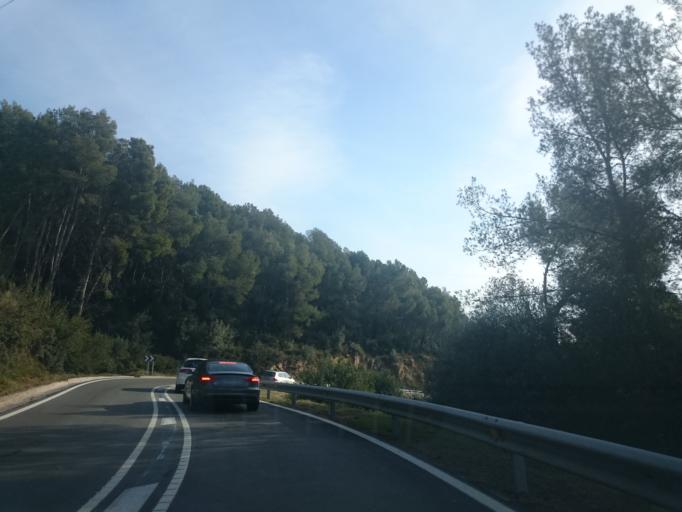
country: ES
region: Catalonia
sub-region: Provincia de Barcelona
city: Gava
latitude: 41.3086
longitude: 1.9809
